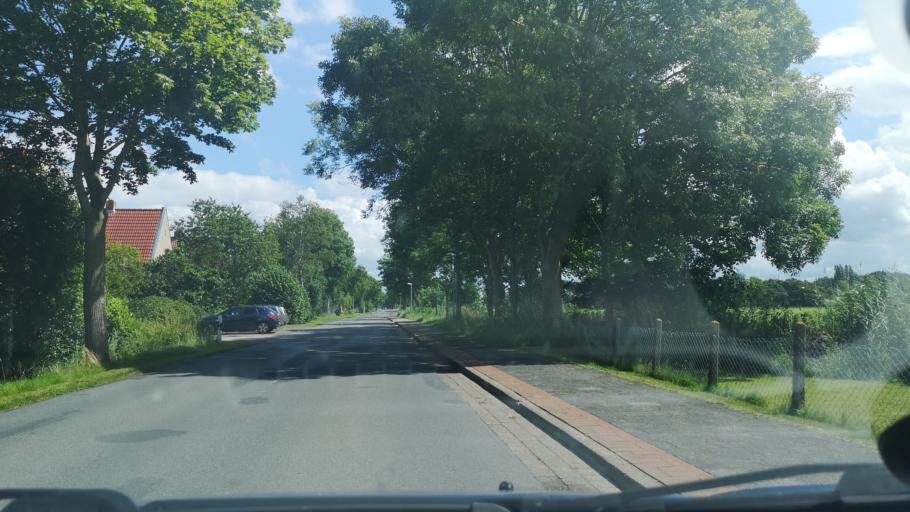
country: DE
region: Lower Saxony
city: Wremen
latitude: 53.6493
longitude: 8.5161
